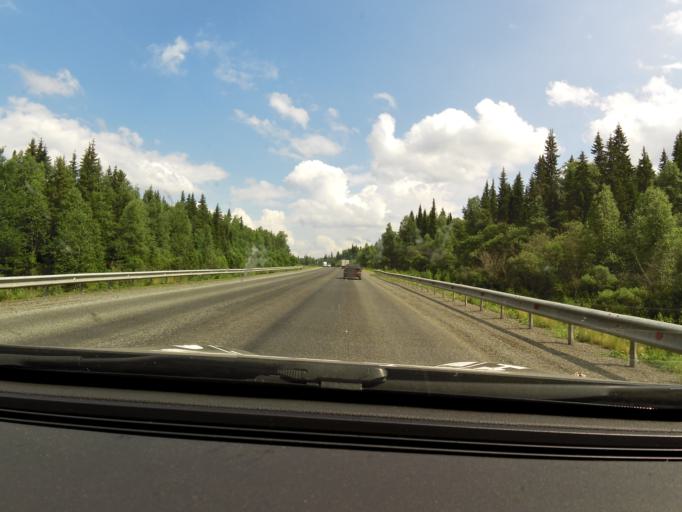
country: RU
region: Sverdlovsk
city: Arti
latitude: 56.7876
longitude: 58.5106
